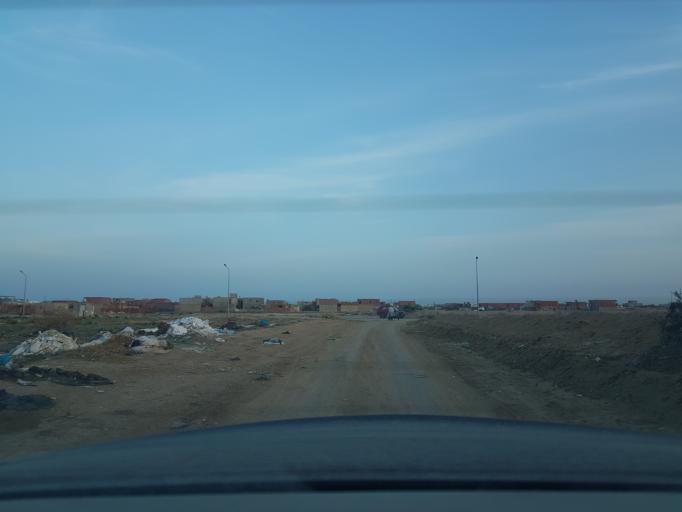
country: TN
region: Safaqis
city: Sfax
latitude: 34.7023
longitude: 10.6979
